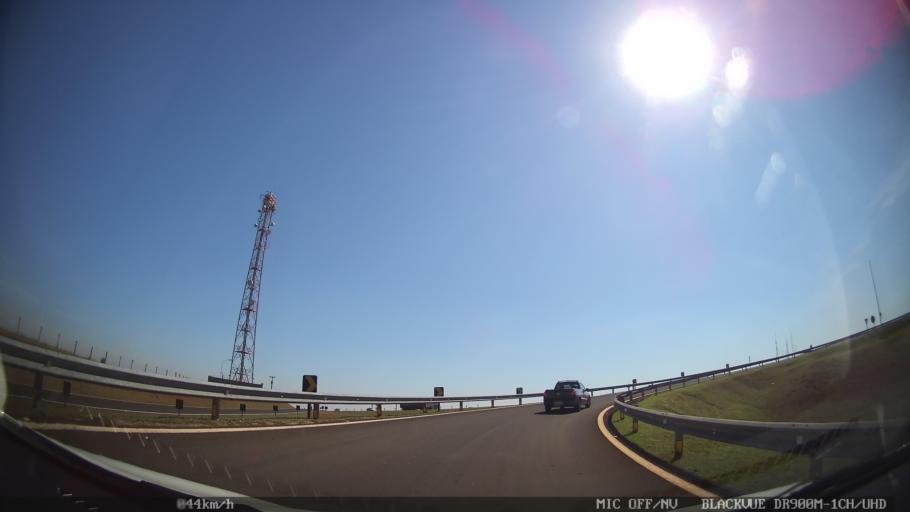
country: BR
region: Sao Paulo
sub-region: Ribeirao Preto
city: Ribeirao Preto
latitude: -21.1673
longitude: -47.9007
